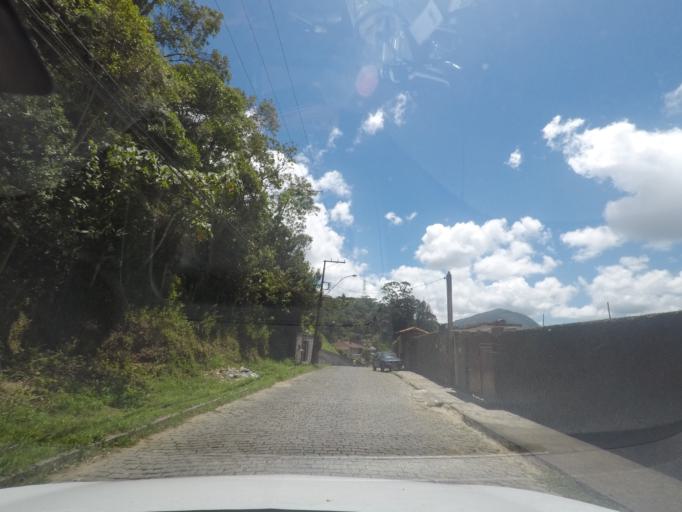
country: BR
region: Rio de Janeiro
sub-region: Teresopolis
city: Teresopolis
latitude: -22.4200
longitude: -42.9839
